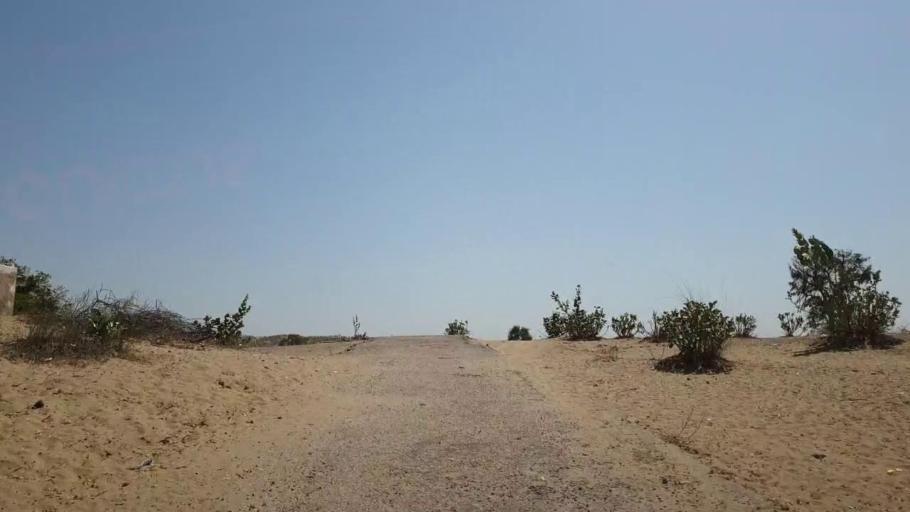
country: PK
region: Sindh
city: Nabisar
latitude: 25.1046
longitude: 69.9041
